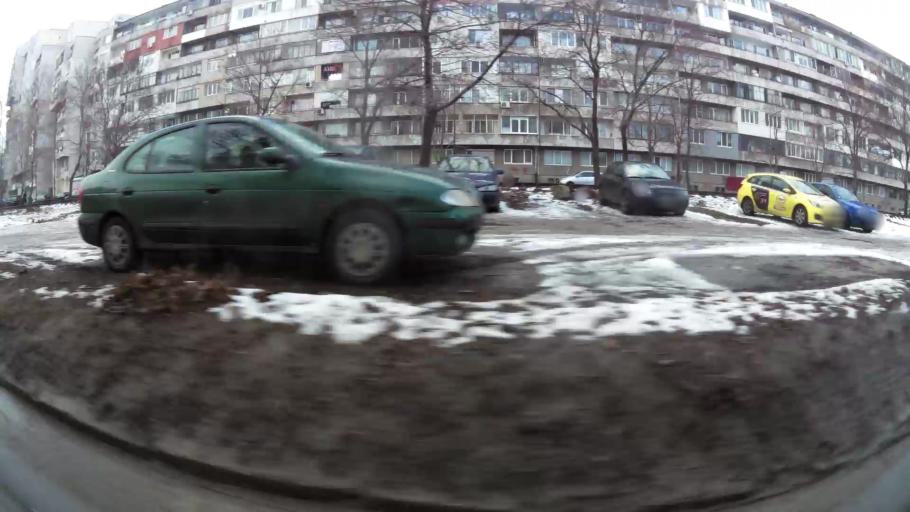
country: BG
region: Sofia-Capital
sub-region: Stolichna Obshtina
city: Sofia
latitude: 42.7006
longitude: 23.2858
